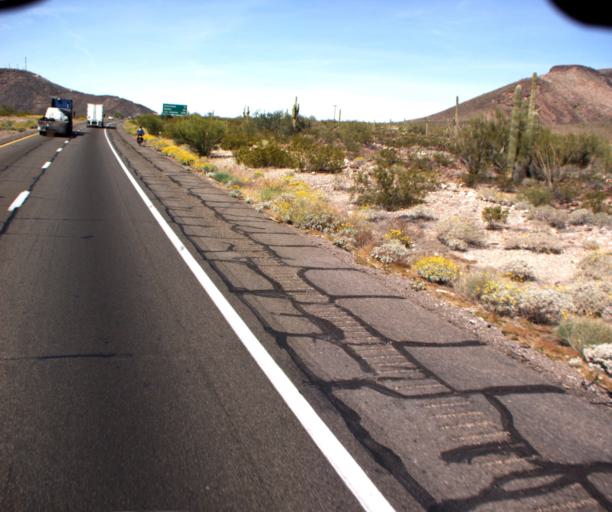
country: US
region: Arizona
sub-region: La Paz County
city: Quartzsite
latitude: 33.6642
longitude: -114.0288
